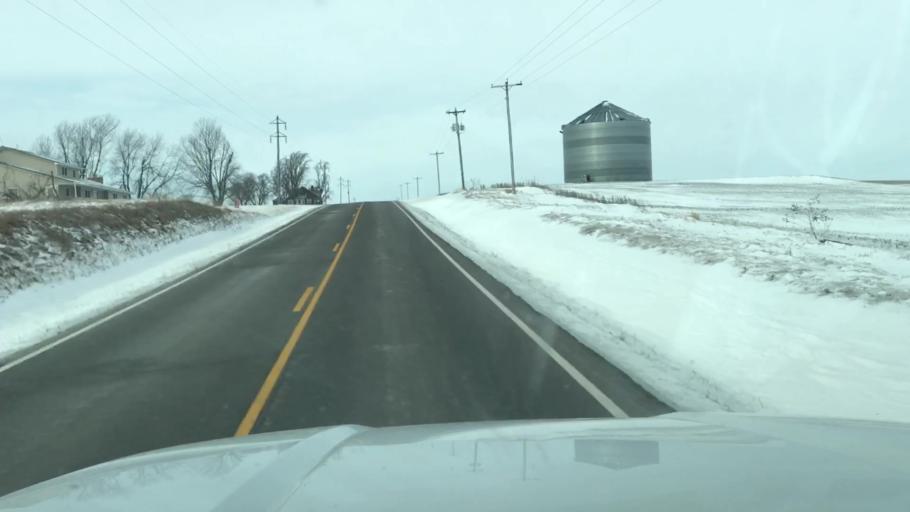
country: US
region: Missouri
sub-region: Holt County
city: Mound City
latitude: 40.1301
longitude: -95.1167
